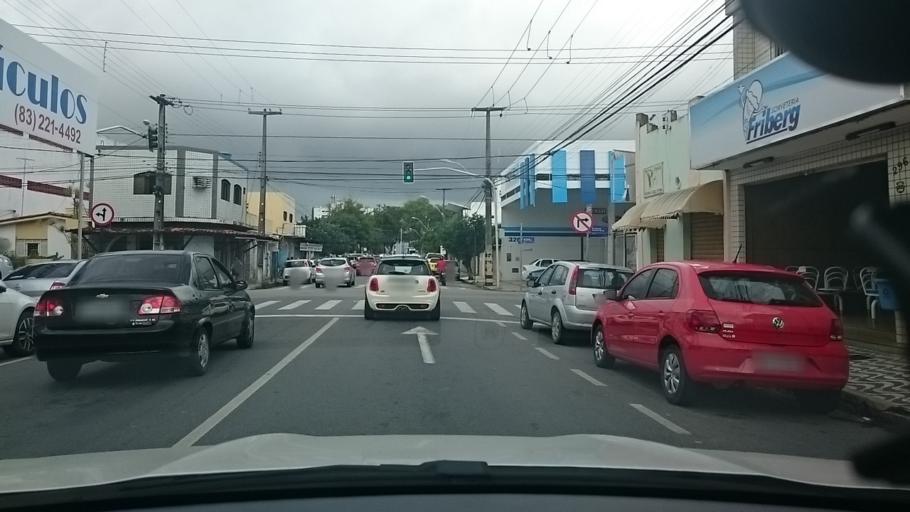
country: BR
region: Paraiba
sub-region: Joao Pessoa
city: Joao Pessoa
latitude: -7.1217
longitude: -34.8686
